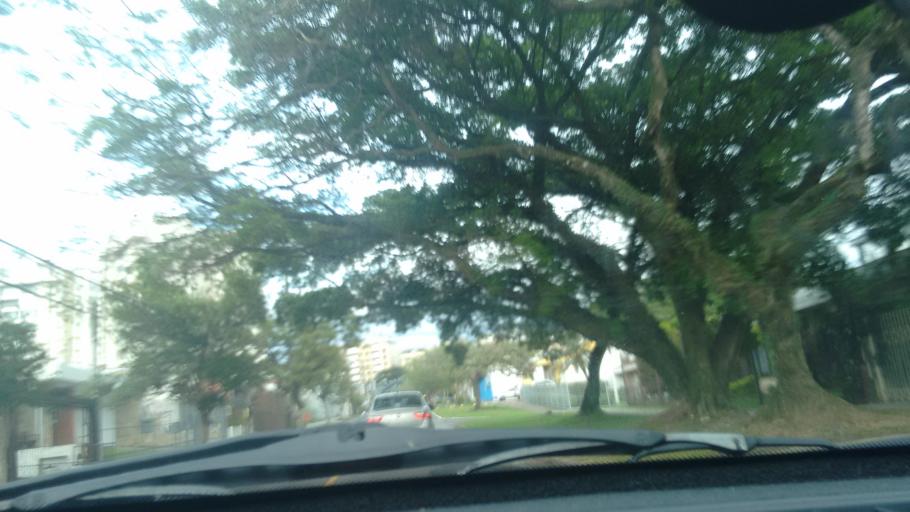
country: BR
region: Rio Grande do Sul
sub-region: Cachoeirinha
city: Cachoeirinha
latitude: -30.0060
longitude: -51.1521
